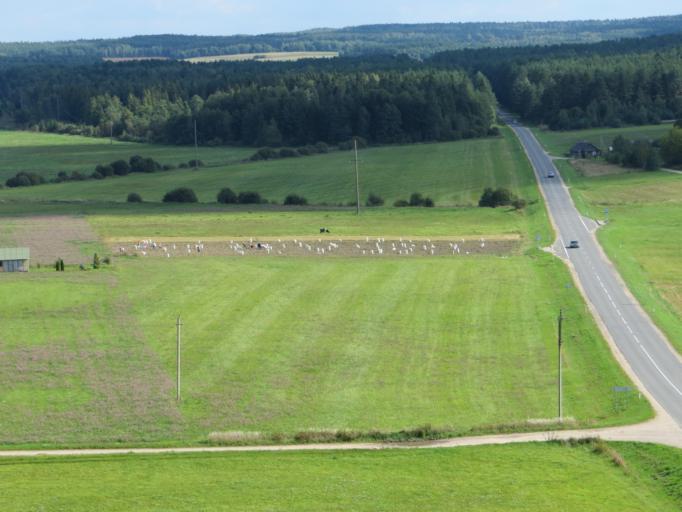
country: LT
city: Salcininkai
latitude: 54.3227
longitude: 25.4686
